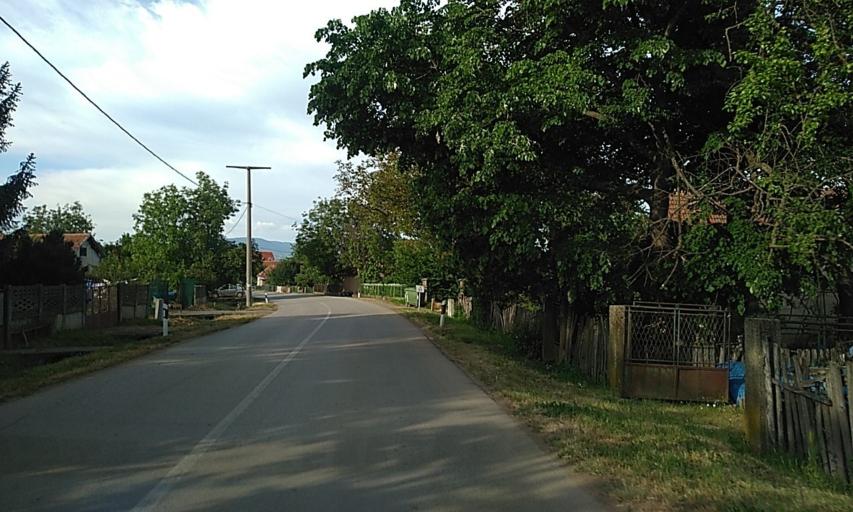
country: RS
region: Central Serbia
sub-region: Nisavski Okrug
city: Aleksinac
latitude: 43.4414
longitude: 21.7343
